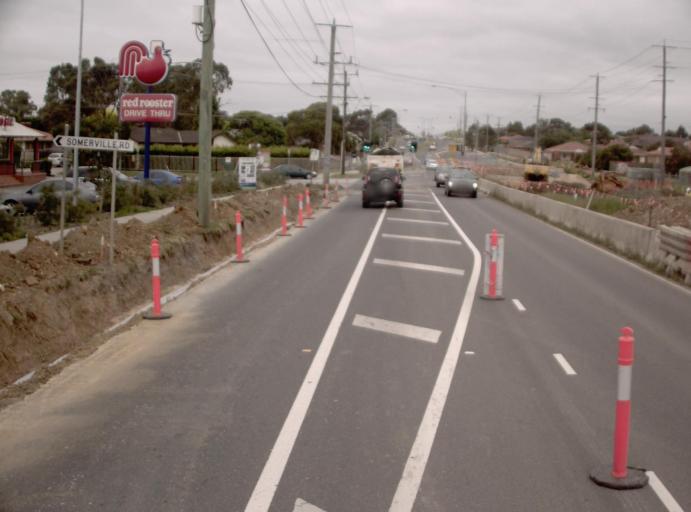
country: AU
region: Victoria
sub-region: Casey
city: Hallam
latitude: -38.0329
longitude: 145.2677
